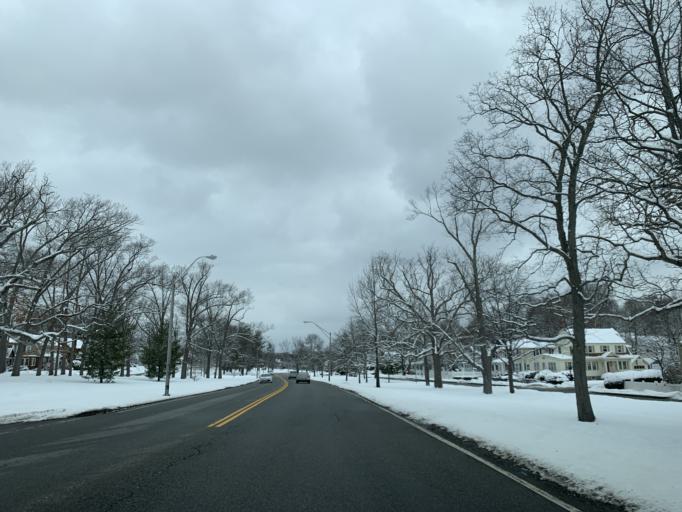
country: US
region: Massachusetts
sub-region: Suffolk County
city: Jamaica Plain
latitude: 42.2804
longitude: -71.1437
